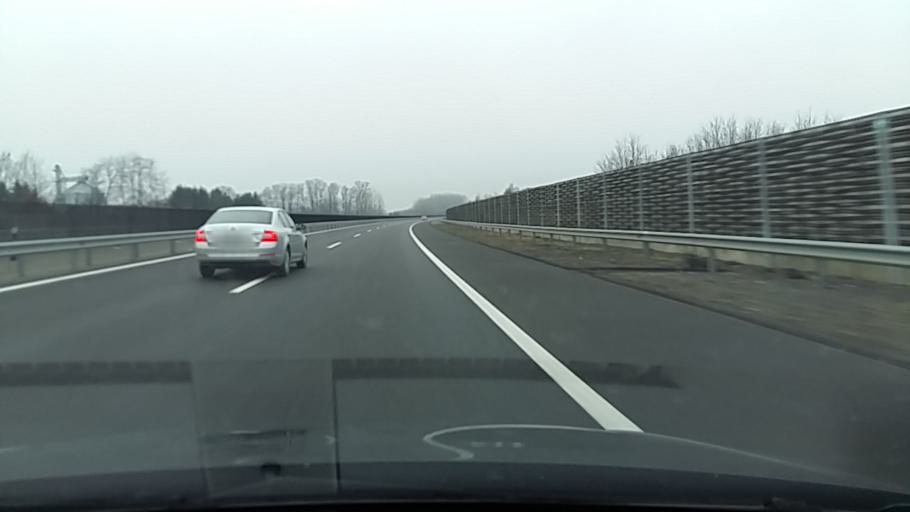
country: HU
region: Szabolcs-Szatmar-Bereg
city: Kalmanhaza
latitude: 47.8962
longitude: 21.6109
